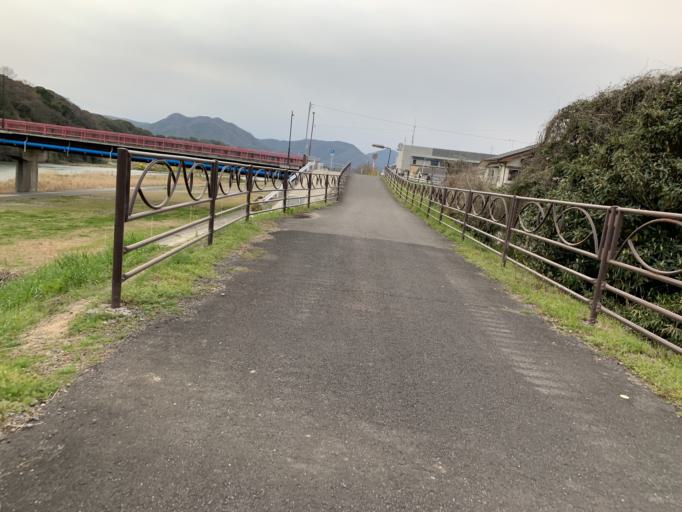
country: JP
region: Oita
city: Bungo-Takada-shi
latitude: 33.5346
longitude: 131.3517
